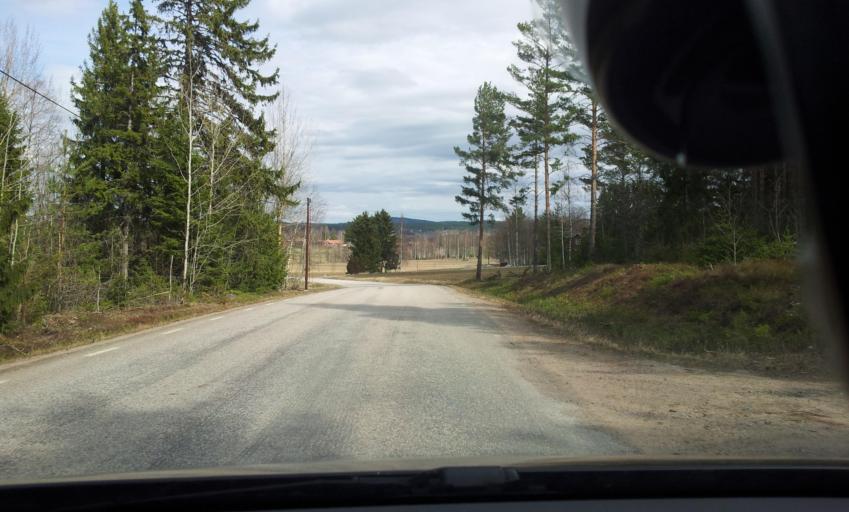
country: SE
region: Gaevleborg
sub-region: Ljusdals Kommun
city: Ljusdal
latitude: 61.8081
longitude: 16.0686
